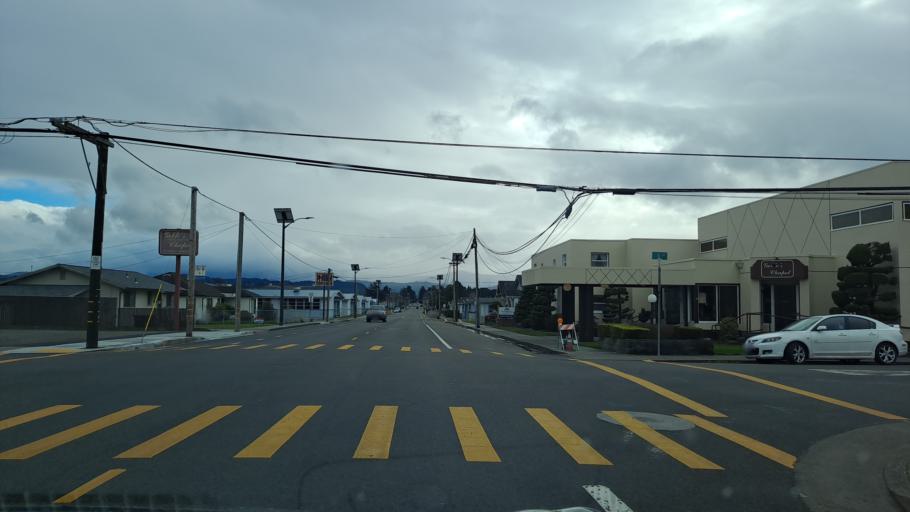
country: US
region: California
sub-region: Humboldt County
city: Fortuna
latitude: 40.5973
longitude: -124.1545
